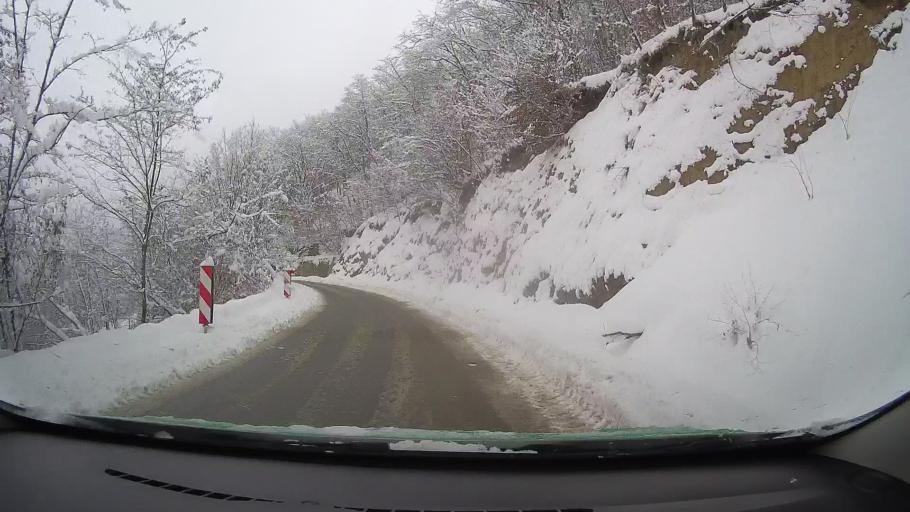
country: RO
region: Alba
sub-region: Comuna Sugag
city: Dobra
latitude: 45.7582
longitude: 23.6641
